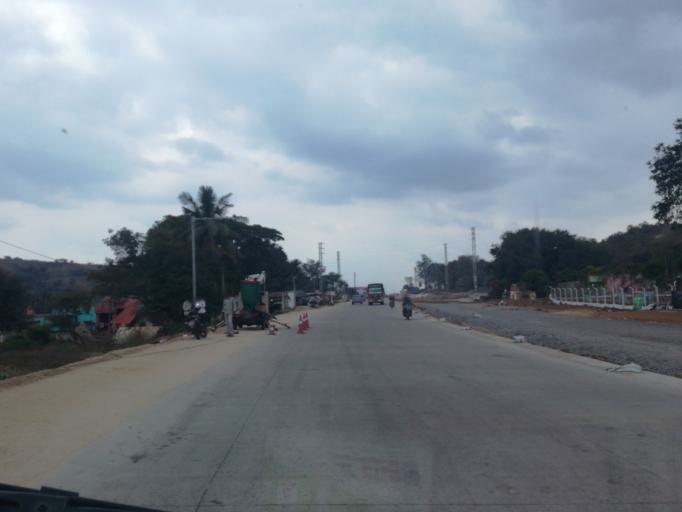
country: IN
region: Andhra Pradesh
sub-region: Chittoor
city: Ramapuram
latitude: 13.0932
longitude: 79.1335
